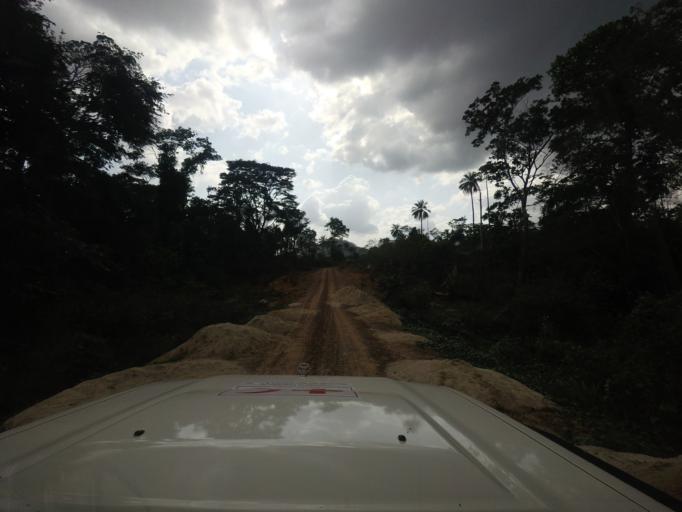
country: LR
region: Lofa
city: Voinjama
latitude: 8.3939
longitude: -9.6485
